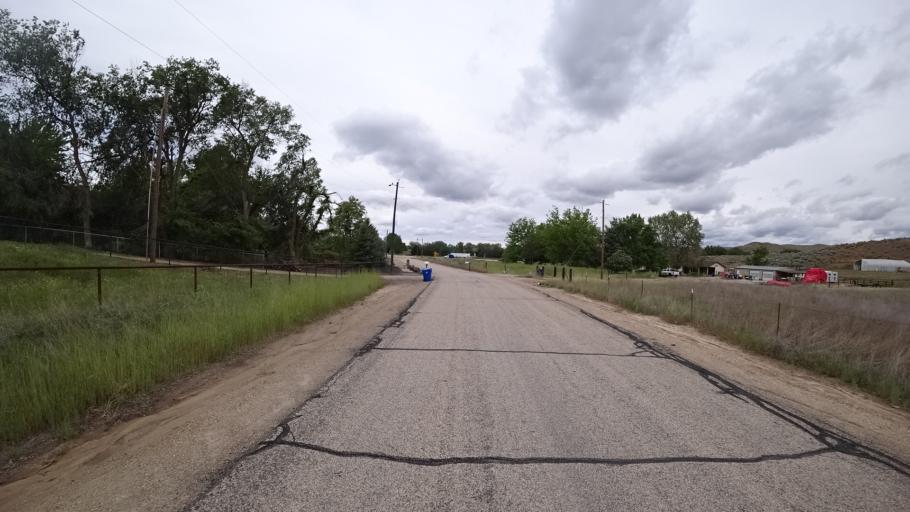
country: US
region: Idaho
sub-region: Ada County
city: Eagle
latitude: 43.7189
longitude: -116.3172
